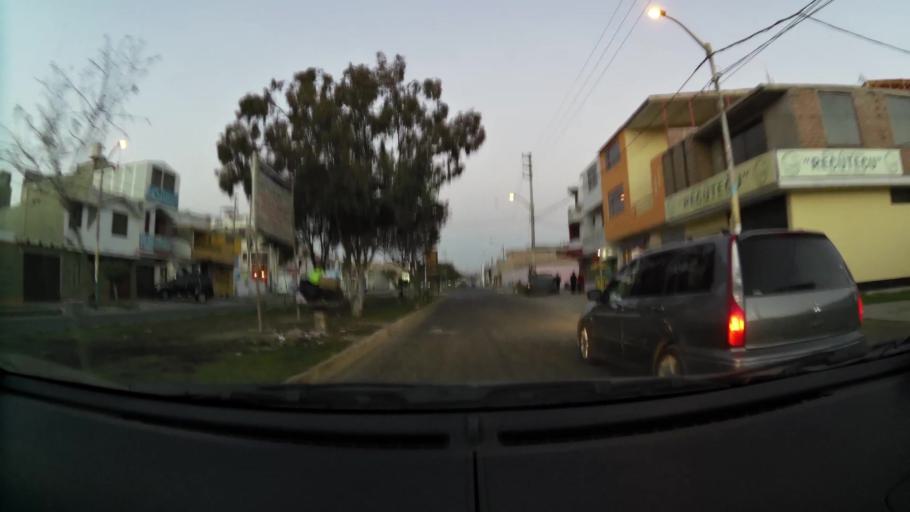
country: PE
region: Ancash
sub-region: Provincia de Santa
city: Buenos Aires
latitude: -9.1230
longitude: -78.5262
